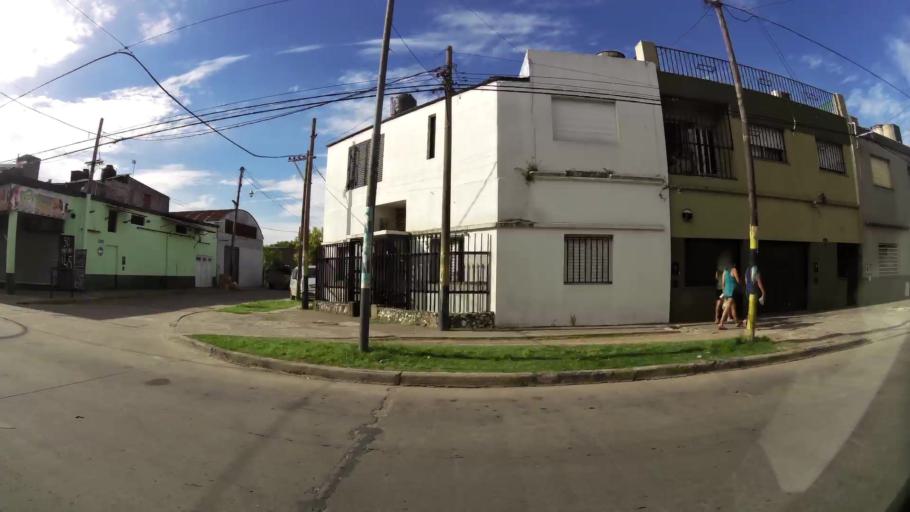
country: AR
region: Santa Fe
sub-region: Departamento de Rosario
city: Rosario
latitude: -32.9271
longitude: -60.6969
